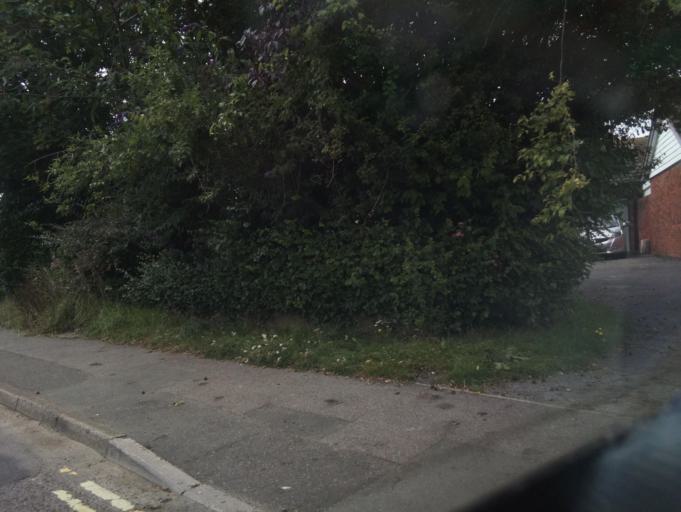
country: GB
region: England
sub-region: Dorset
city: Blandford Forum
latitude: 50.8649
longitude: -2.1557
